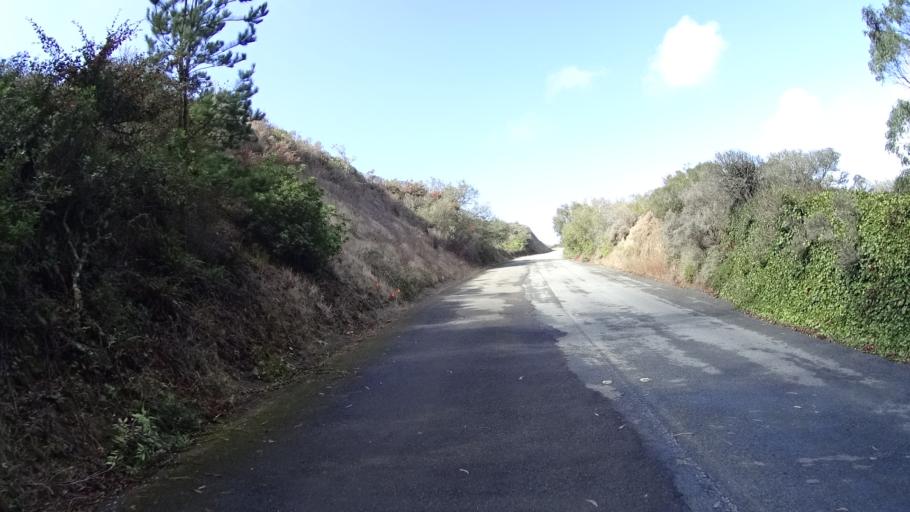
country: US
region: California
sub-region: San Mateo County
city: Daly City
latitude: 37.6942
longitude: -122.4381
